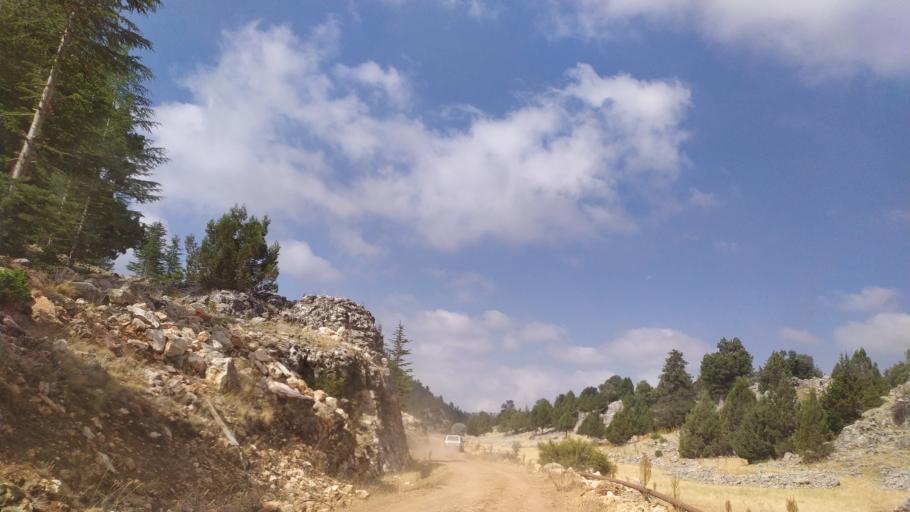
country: TR
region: Mersin
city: Kirobasi
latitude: 36.6189
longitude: 33.8381
